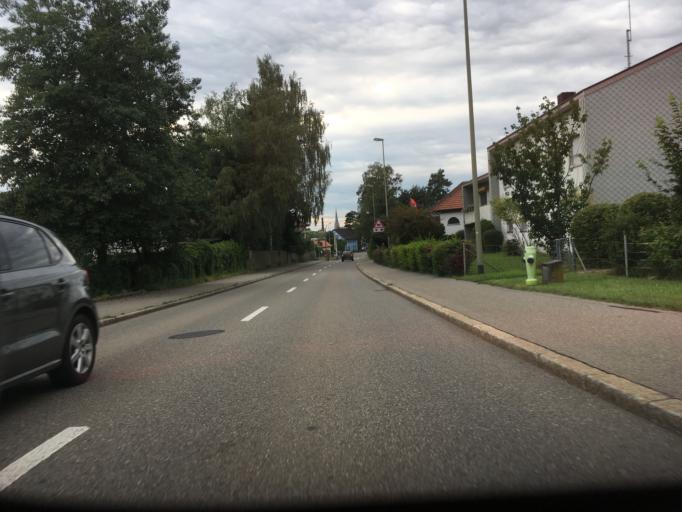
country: CH
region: Zurich
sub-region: Bezirk Pfaeffikon
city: Pfaffikon
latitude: 47.3647
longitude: 8.7905
